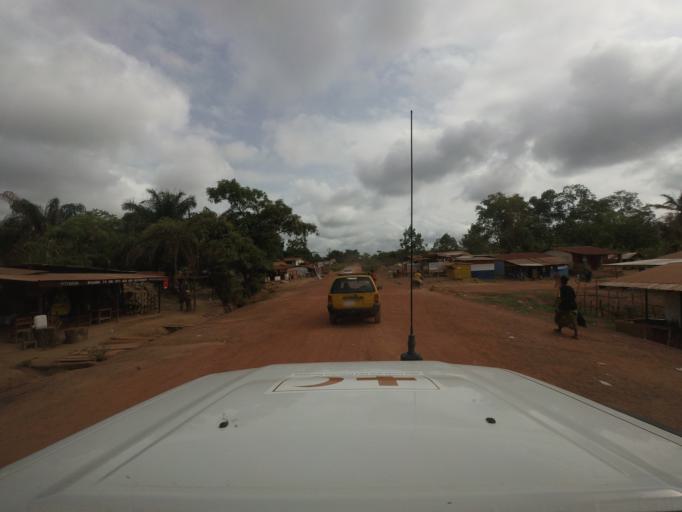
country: LR
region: Bong
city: Gbarnga
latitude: 7.0094
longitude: -9.4791
